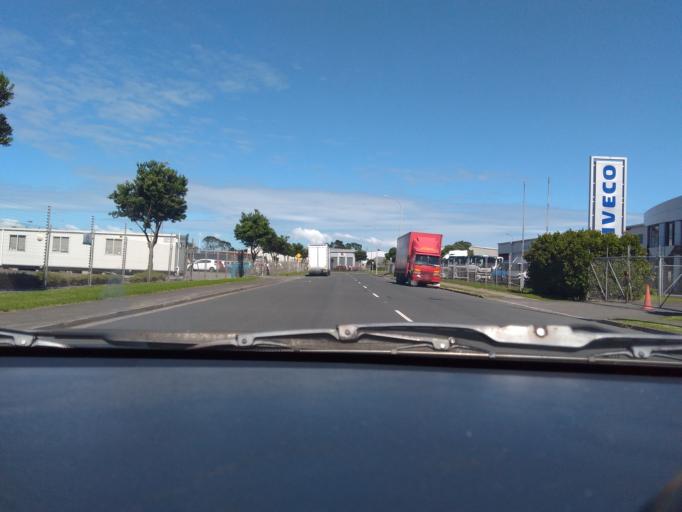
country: NZ
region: Auckland
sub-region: Auckland
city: Wiri
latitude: -37.0026
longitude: 174.8507
